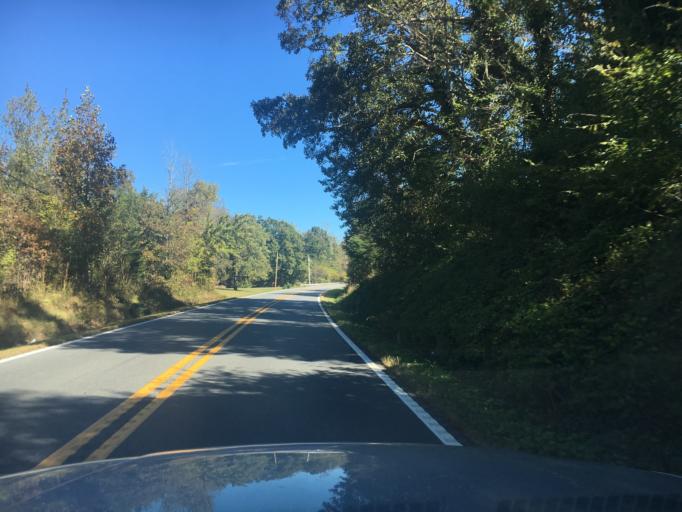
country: US
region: North Carolina
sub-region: Rutherford County
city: Spindale
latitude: 35.4806
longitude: -81.8792
